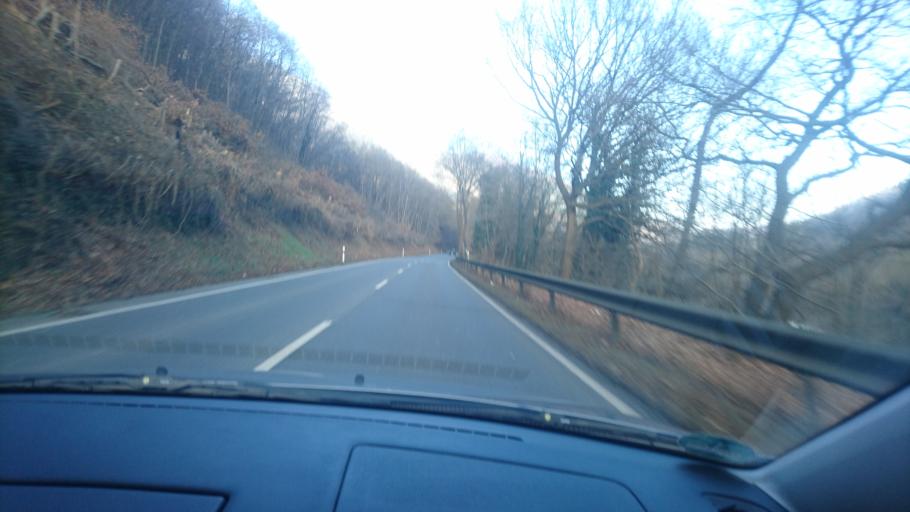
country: DE
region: Rheinland-Pfalz
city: Miellen
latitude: 50.3151
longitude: 7.6488
